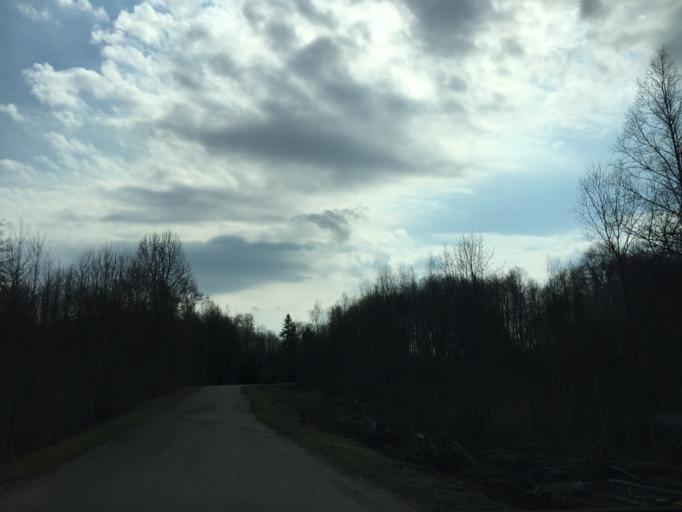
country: LV
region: Aluksnes Rajons
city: Aluksne
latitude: 57.5542
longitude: 26.9009
